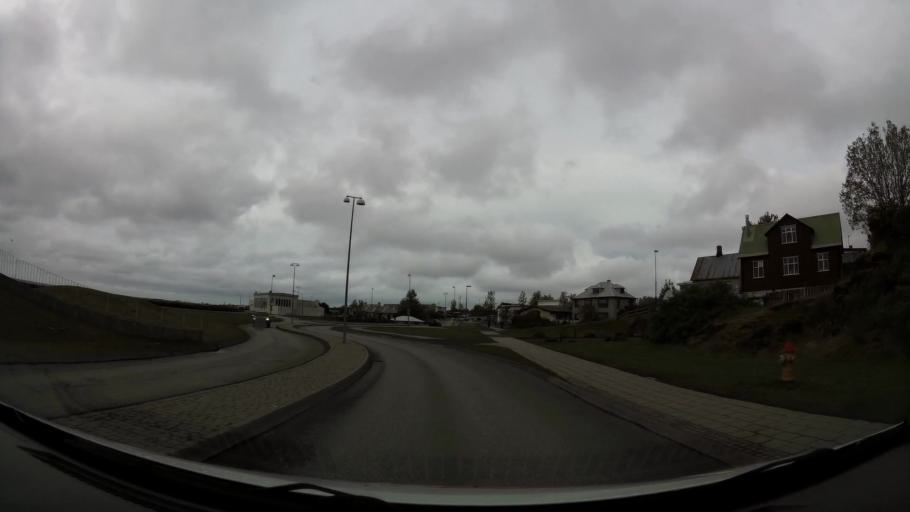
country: IS
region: Capital Region
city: Hafnarfjoerdur
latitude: 64.0710
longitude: -21.9657
